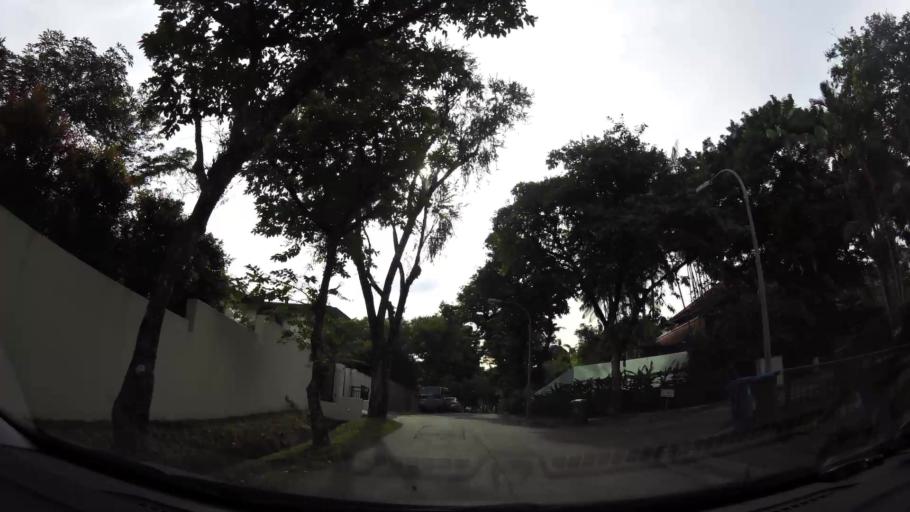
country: SG
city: Singapore
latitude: 1.3267
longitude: 103.8171
